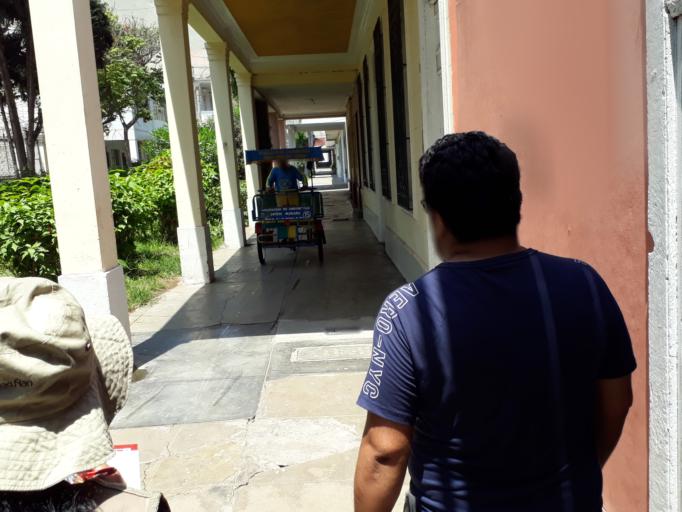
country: PE
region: Lima
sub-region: Lima
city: Santa Rosa
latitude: -11.7749
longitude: -77.1762
